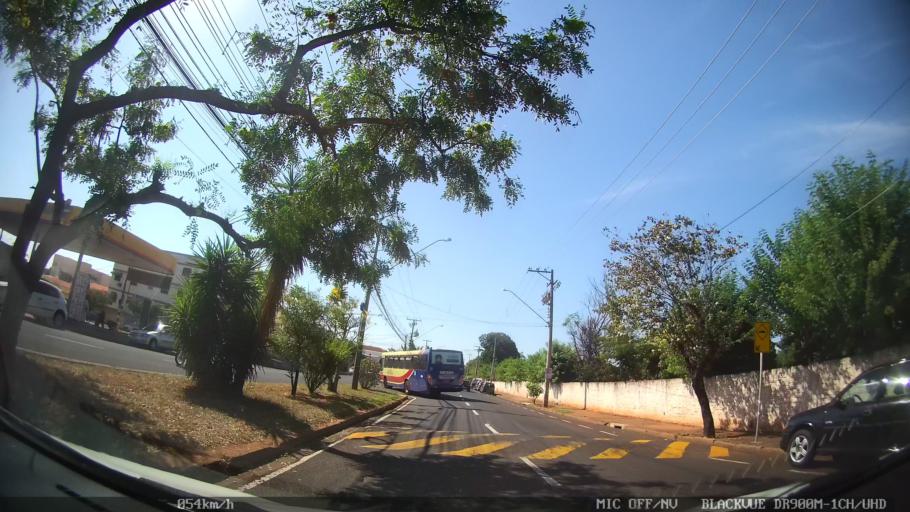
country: BR
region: Sao Paulo
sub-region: Sao Jose Do Rio Preto
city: Sao Jose do Rio Preto
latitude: -20.8099
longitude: -49.4088
